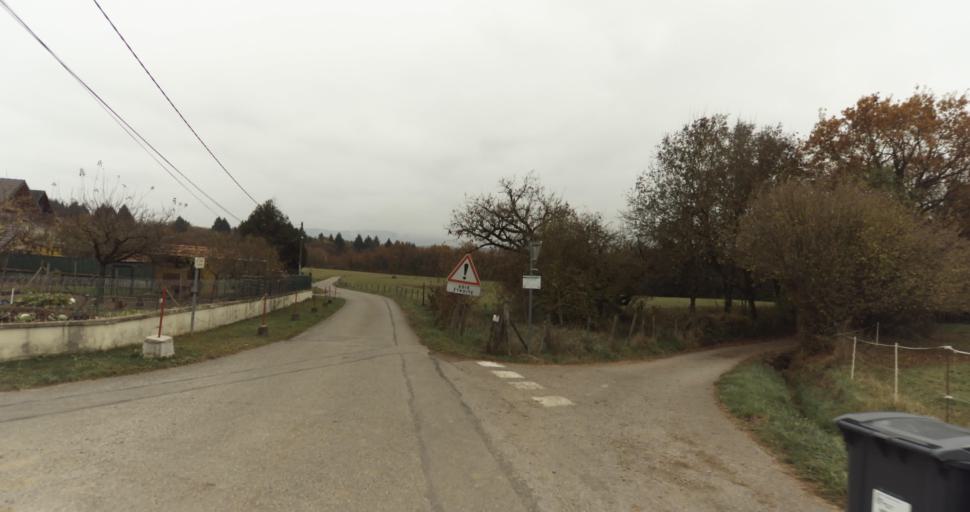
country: FR
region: Rhone-Alpes
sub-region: Departement de la Haute-Savoie
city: Poisy
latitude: 45.9096
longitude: 6.0520
